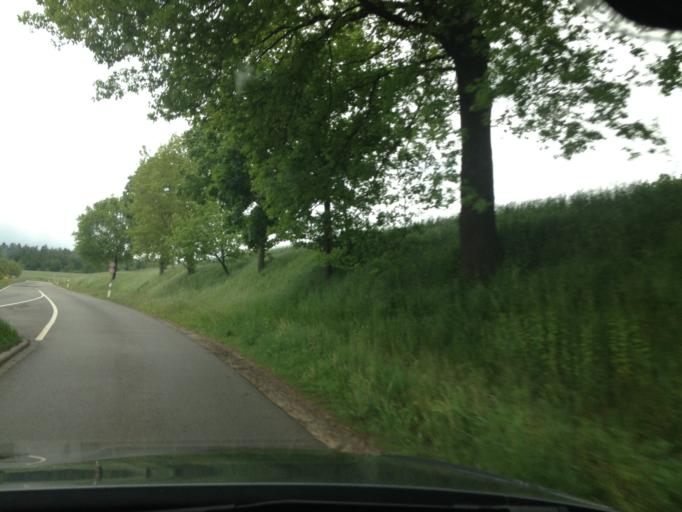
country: DE
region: Saarland
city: Kirkel
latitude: 49.3022
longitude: 7.2083
